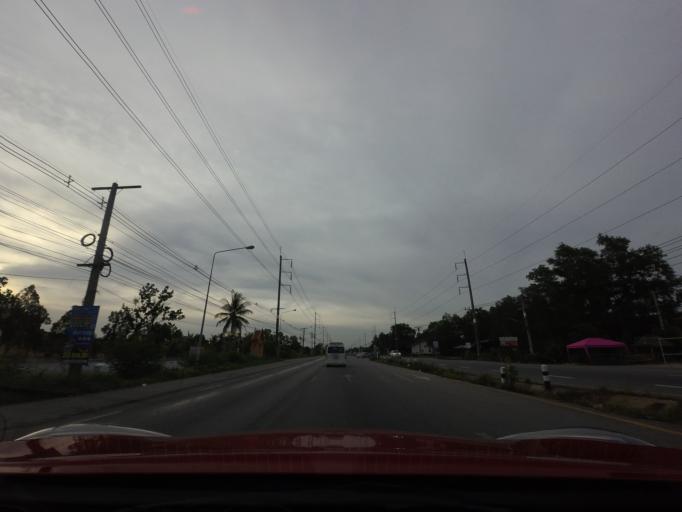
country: TH
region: Songkhla
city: Chana
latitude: 6.9606
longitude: 100.6881
